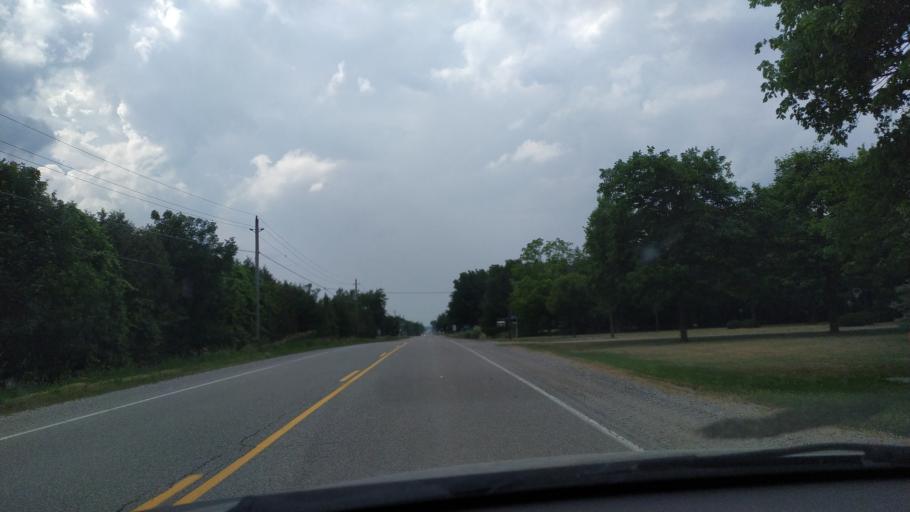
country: CA
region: Ontario
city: Dorchester
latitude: 43.1894
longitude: -81.1470
